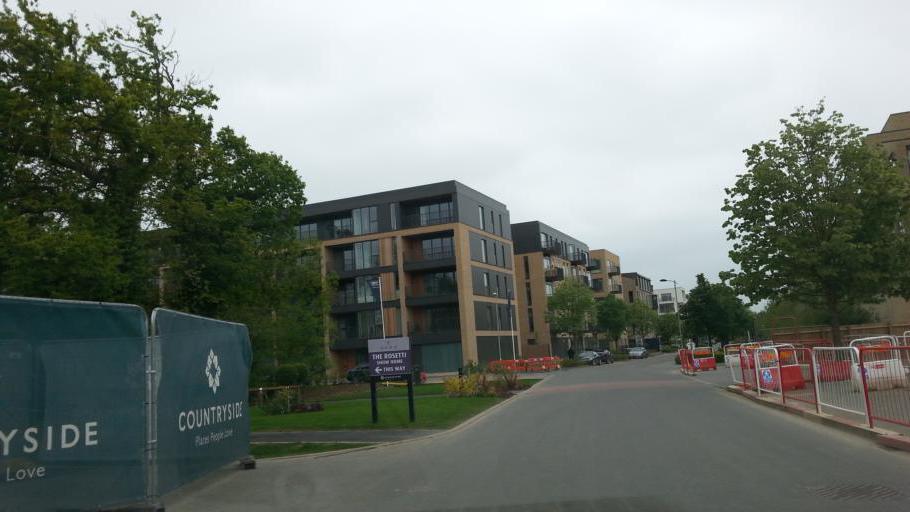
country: GB
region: England
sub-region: Cambridgeshire
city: Cambridge
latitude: 52.1769
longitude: 0.1226
